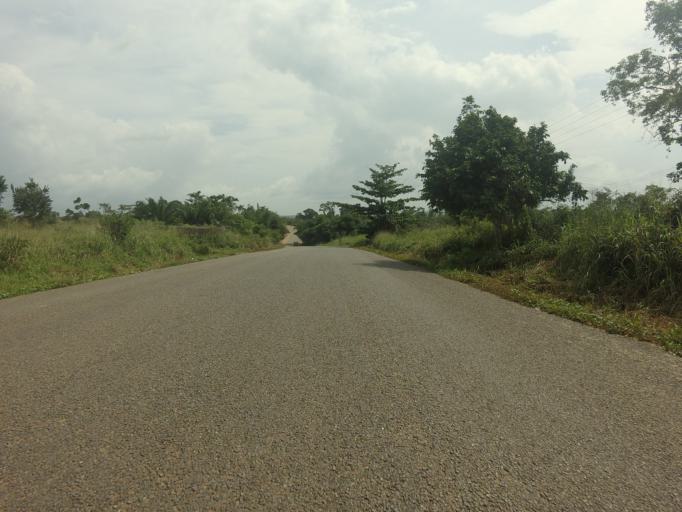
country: GH
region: Eastern
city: Koforidua
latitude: 5.9725
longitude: -0.2271
